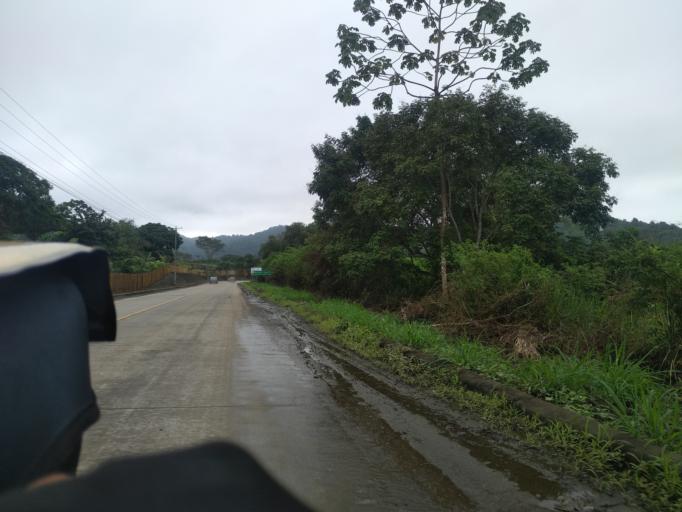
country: EC
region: Manabi
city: Jipijapa
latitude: -1.6692
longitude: -80.8092
